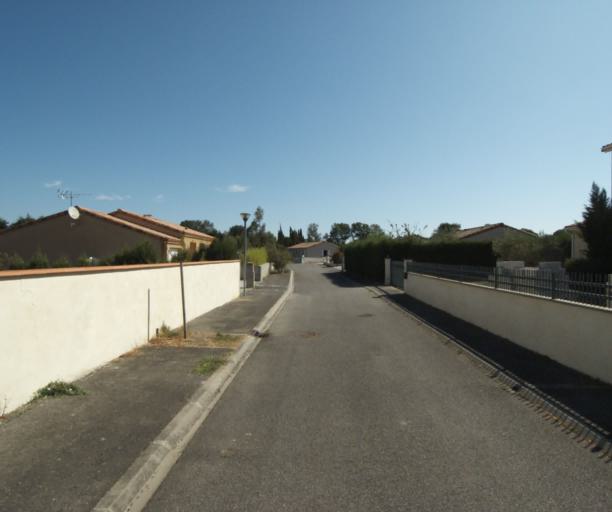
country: FR
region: Midi-Pyrenees
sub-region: Departement du Tarn
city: Soreze
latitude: 43.4522
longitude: 2.0401
